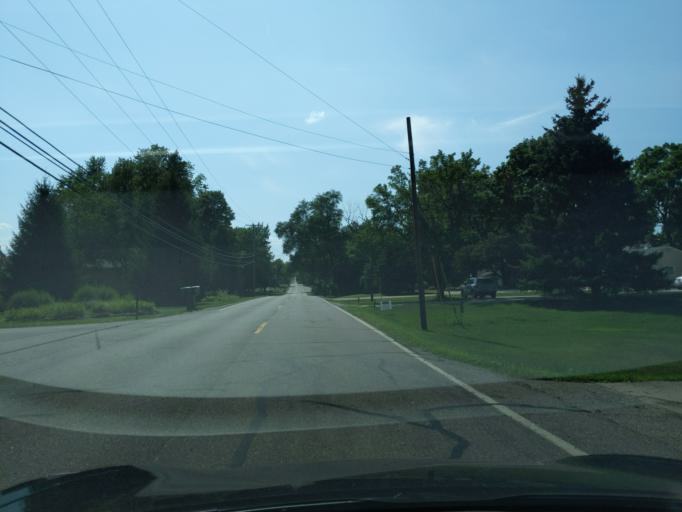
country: US
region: Michigan
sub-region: Eaton County
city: Grand Ledge
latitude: 42.7496
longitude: -84.7238
